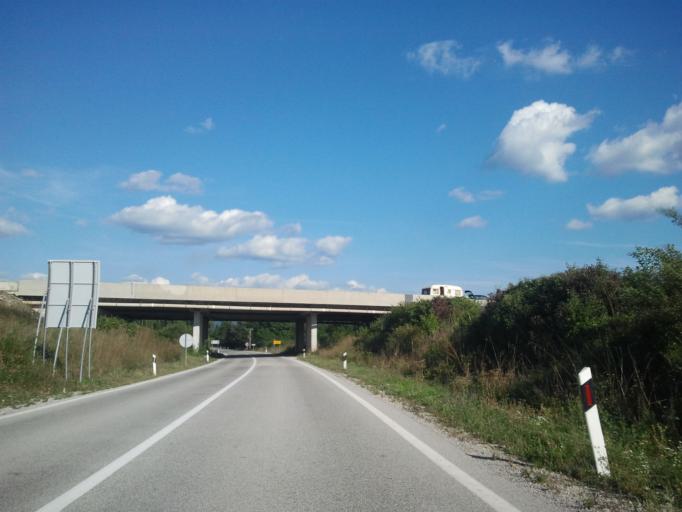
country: HR
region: Zadarska
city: Obrovac
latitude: 44.3850
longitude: 15.6295
